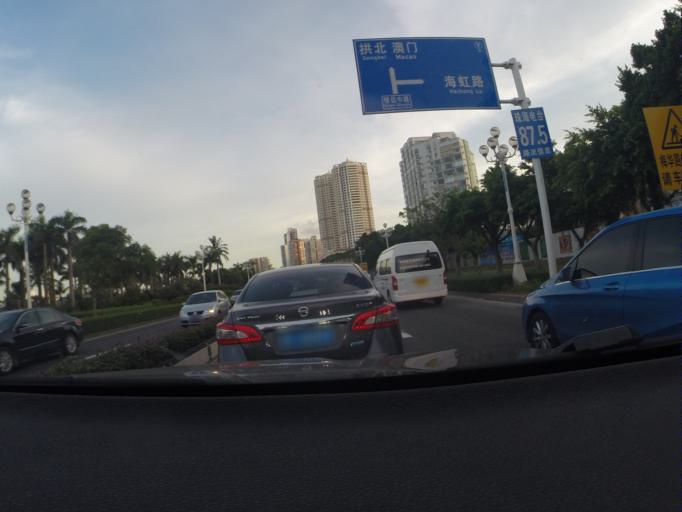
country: CN
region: Guangdong
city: Zhuhai
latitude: 22.2963
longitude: 113.5729
